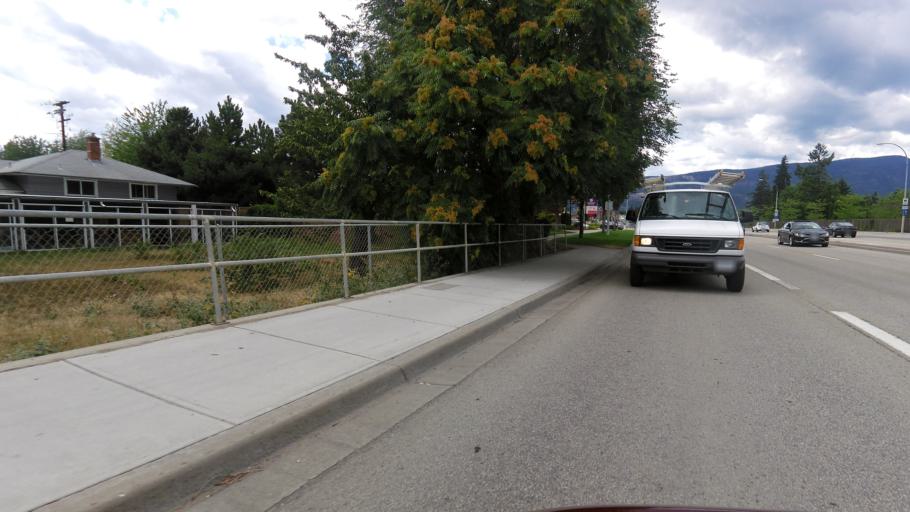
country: CA
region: British Columbia
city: Kelowna
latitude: 49.8828
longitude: -119.4722
